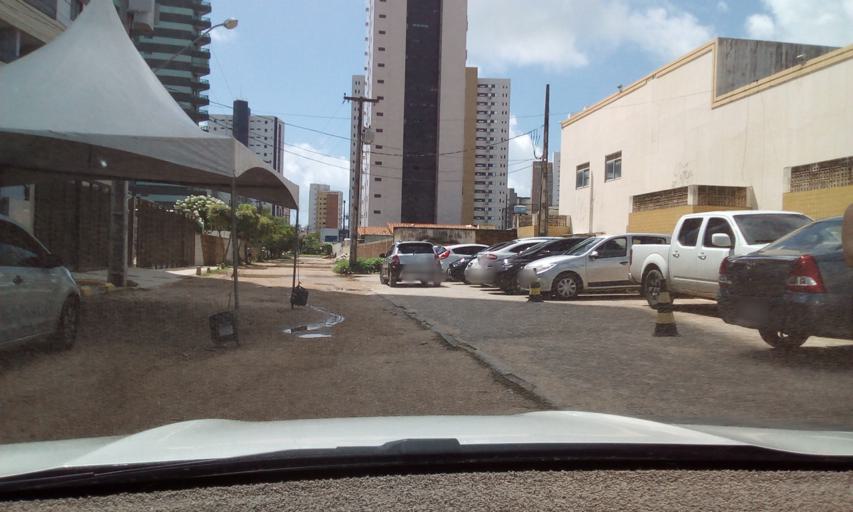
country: BR
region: Paraiba
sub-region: Joao Pessoa
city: Joao Pessoa
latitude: -7.0837
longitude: -34.8417
